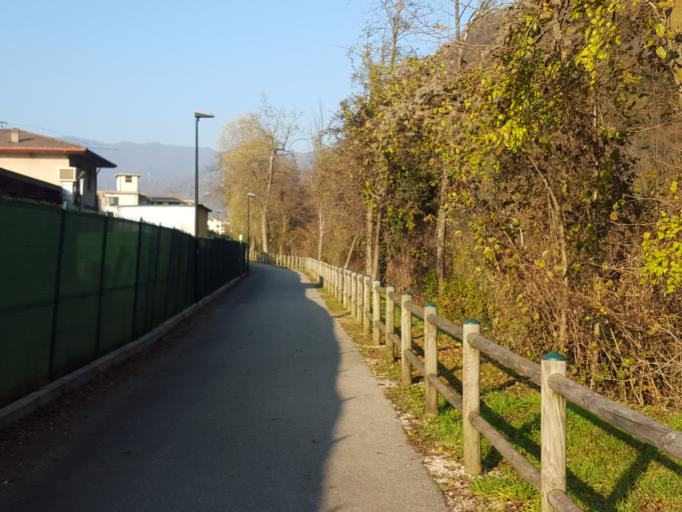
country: IT
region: Veneto
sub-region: Provincia di Vicenza
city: Valdagno
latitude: 45.6371
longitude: 11.3094
